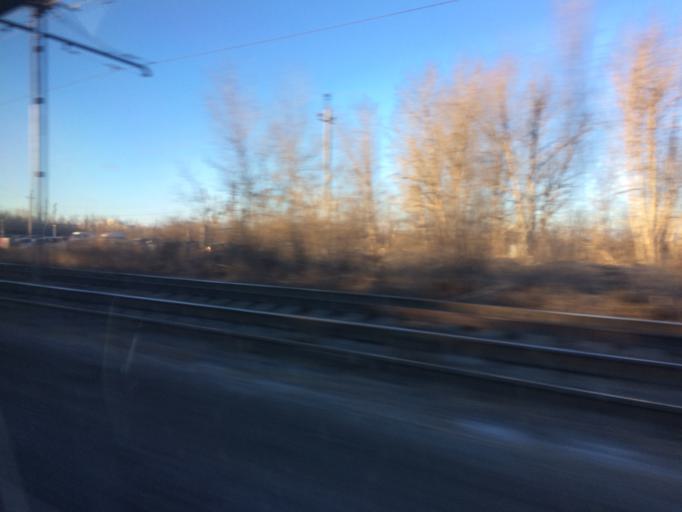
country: RU
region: Chelyabinsk
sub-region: Gorod Magnitogorsk
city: Magnitogorsk
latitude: 53.4065
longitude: 59.0294
